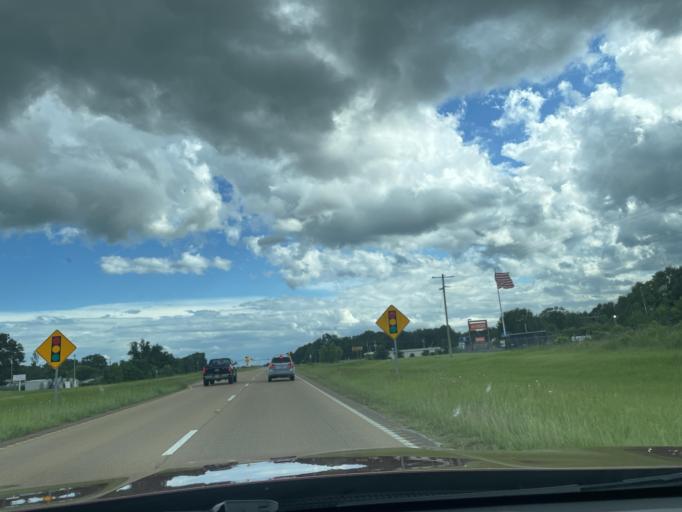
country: US
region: Mississippi
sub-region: Madison County
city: Flora
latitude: 32.5551
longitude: -90.3215
